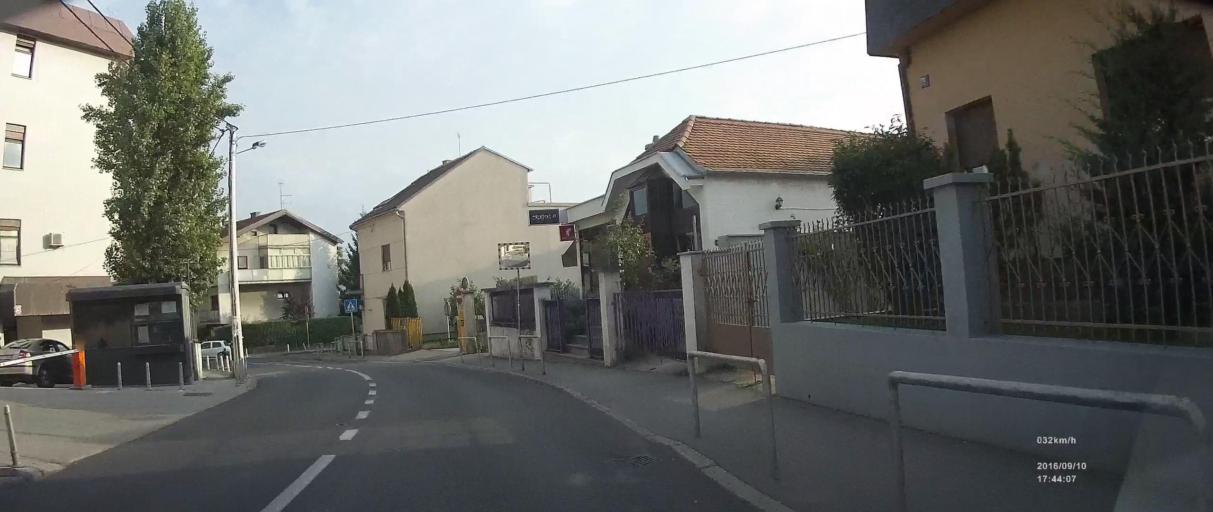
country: HR
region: Grad Zagreb
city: Zagreb - Centar
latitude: 45.8204
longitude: 15.9380
